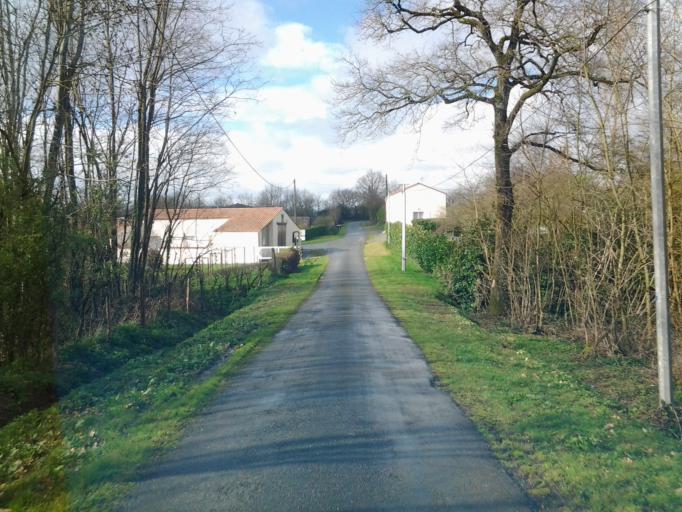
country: FR
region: Pays de la Loire
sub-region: Departement de la Vendee
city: Nesmy
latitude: 46.6459
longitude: -1.3631
